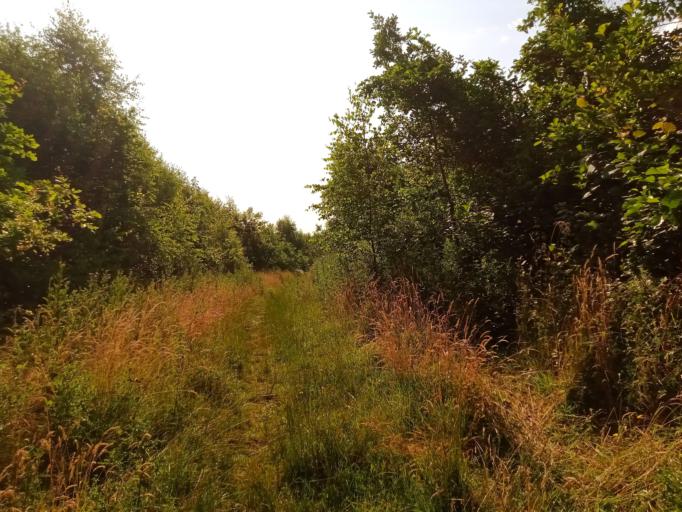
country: IE
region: Leinster
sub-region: Laois
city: Abbeyleix
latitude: 52.9058
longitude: -7.3575
